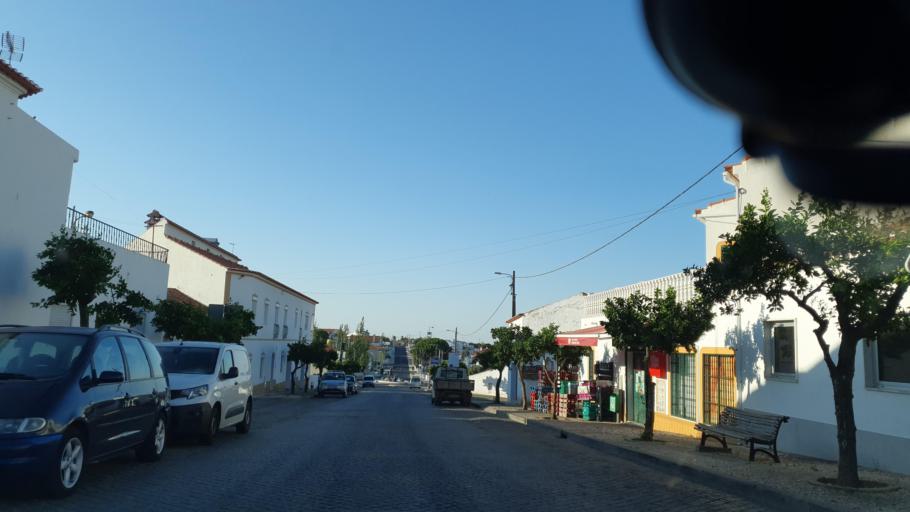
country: PT
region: Portalegre
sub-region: Fronteira
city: Fronteira
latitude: 38.9558
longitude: -7.6746
